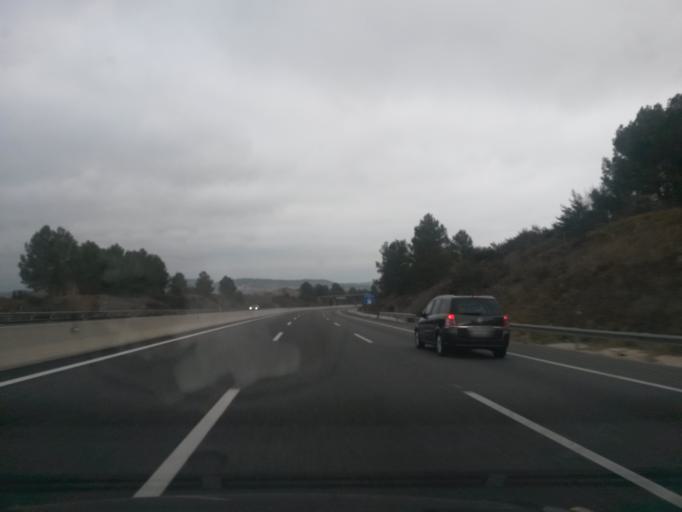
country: ES
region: Catalonia
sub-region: Provincia de Girona
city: Bascara
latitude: 42.1534
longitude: 2.9172
